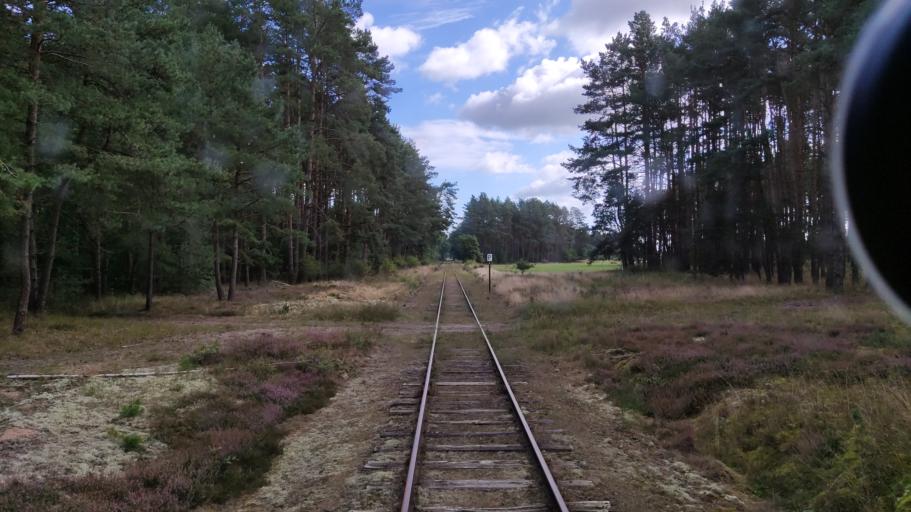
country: DE
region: Lower Saxony
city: Bleckede
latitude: 53.2886
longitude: 10.6966
